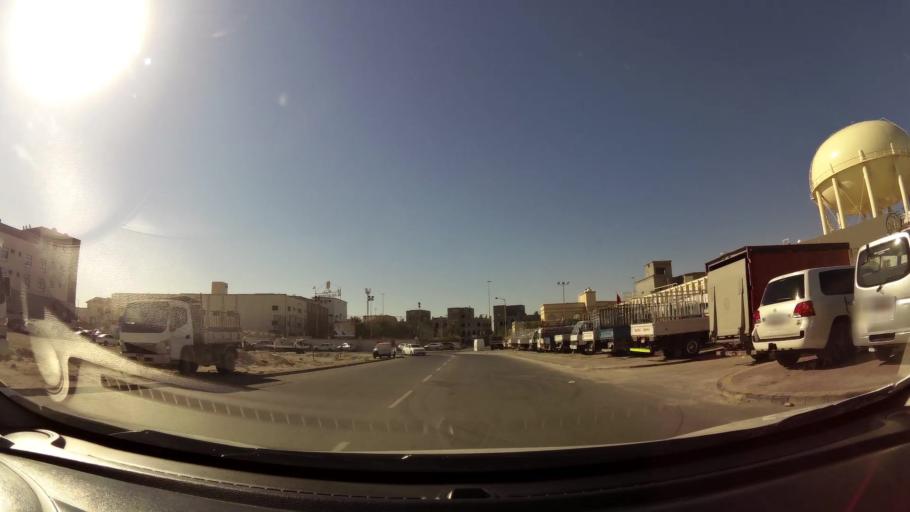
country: BH
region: Muharraq
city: Al Muharraq
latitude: 26.2539
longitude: 50.6059
